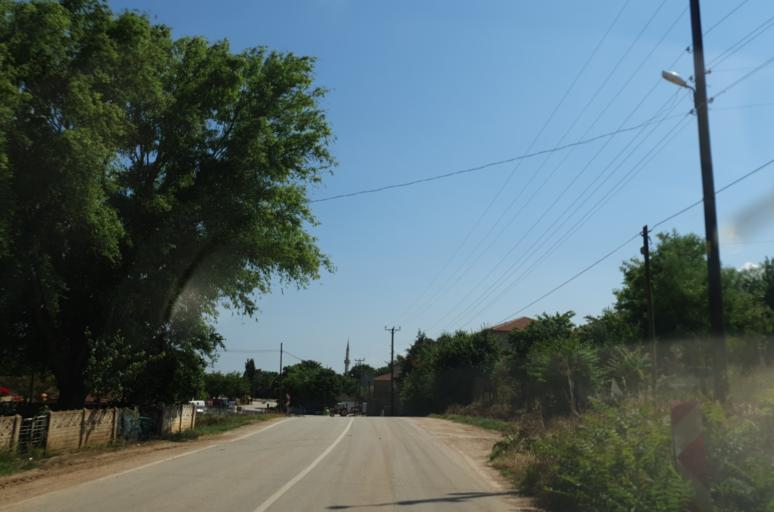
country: TR
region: Kirklareli
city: Vize
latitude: 41.4903
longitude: 27.6943
